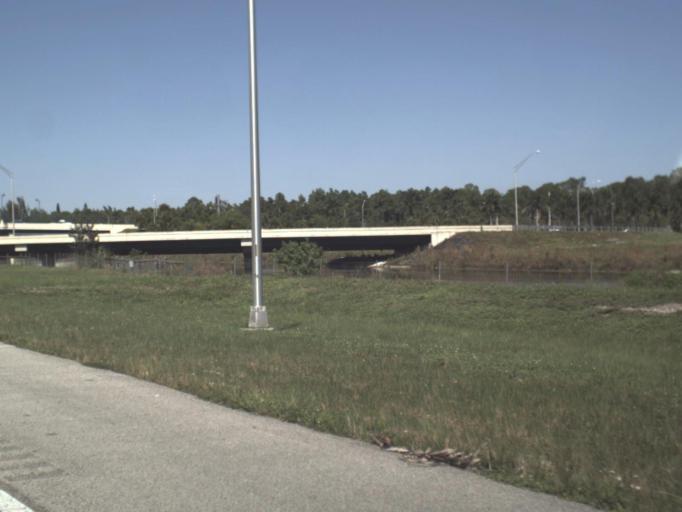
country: US
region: Florida
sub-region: Collier County
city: Golden Gate
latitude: 26.1717
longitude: -81.7327
